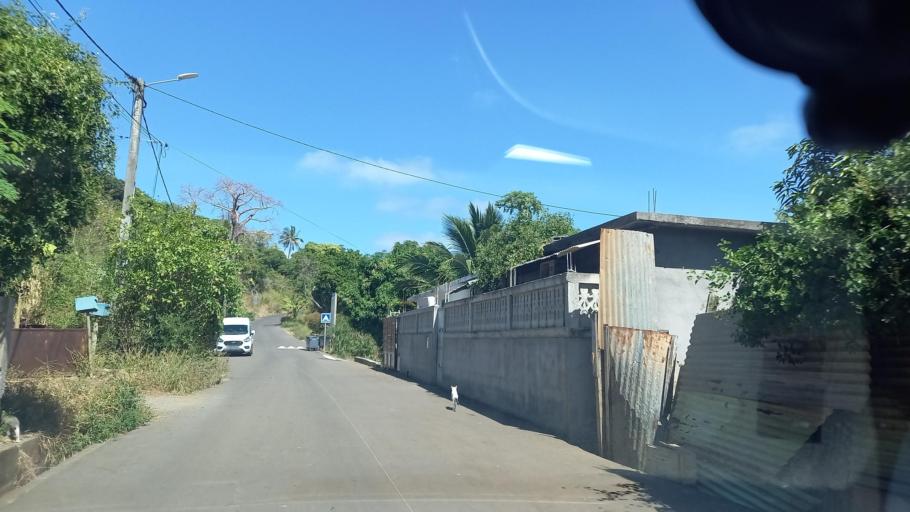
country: YT
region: Kani-Keli
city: Kani Keli
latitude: -12.9661
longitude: 45.1116
